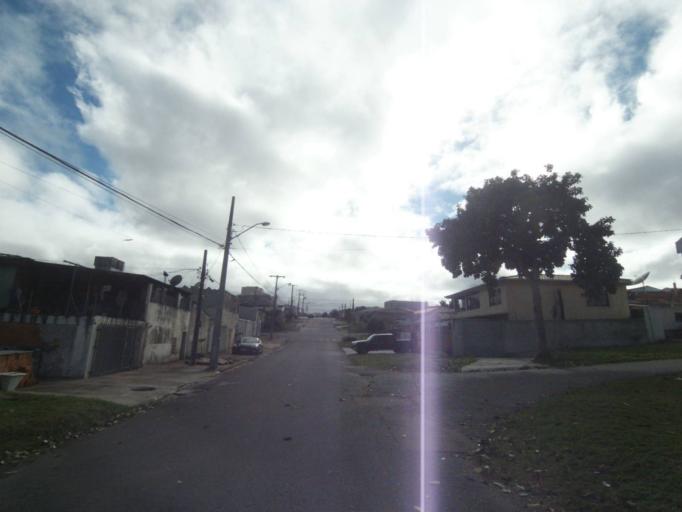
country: BR
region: Parana
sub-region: Sao Jose Dos Pinhais
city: Sao Jose dos Pinhais
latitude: -25.5217
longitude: -49.3037
